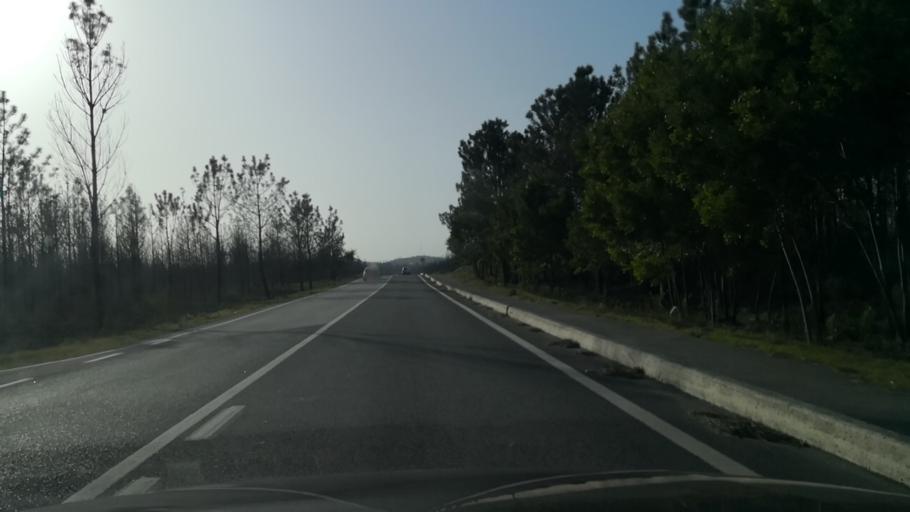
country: PT
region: Leiria
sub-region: Marinha Grande
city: Marinha Grande
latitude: 39.7474
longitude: -8.9588
